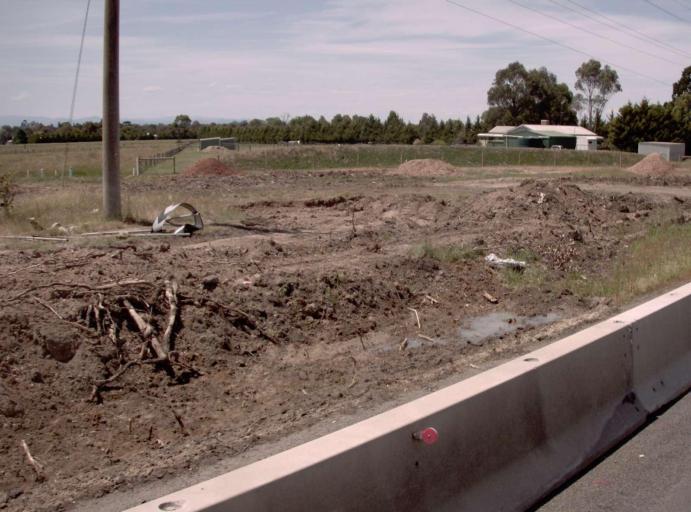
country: AU
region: Victoria
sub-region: Latrobe
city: Traralgon
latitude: -38.1854
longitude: 146.5926
